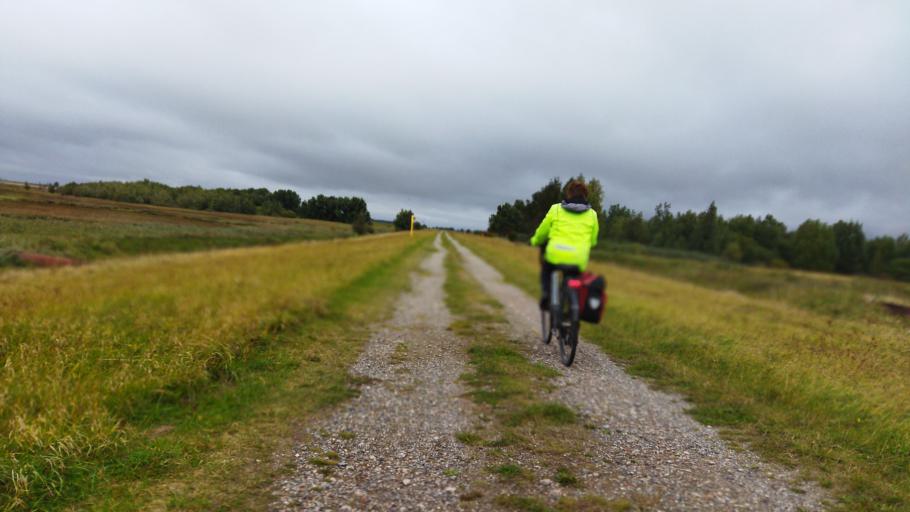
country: NL
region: Groningen
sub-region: Gemeente Delfzijl
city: Delfzijl
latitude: 53.3744
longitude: 7.0113
